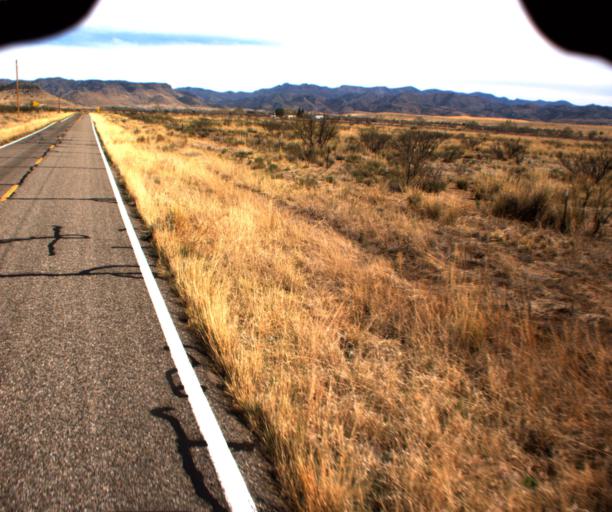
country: US
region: Arizona
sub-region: Cochise County
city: Willcox
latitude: 32.0237
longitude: -109.4457
